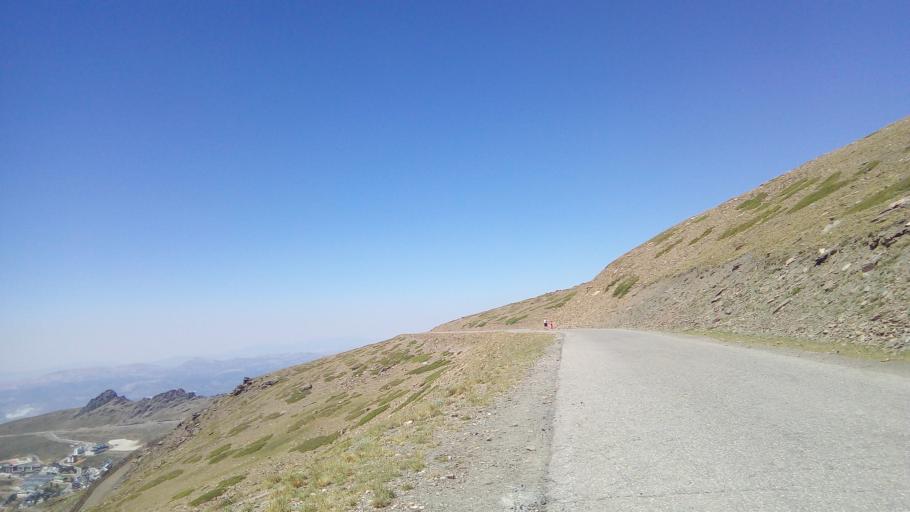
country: ES
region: Andalusia
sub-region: Provincia de Granada
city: Guejar-Sierra
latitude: 37.0778
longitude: -3.3840
